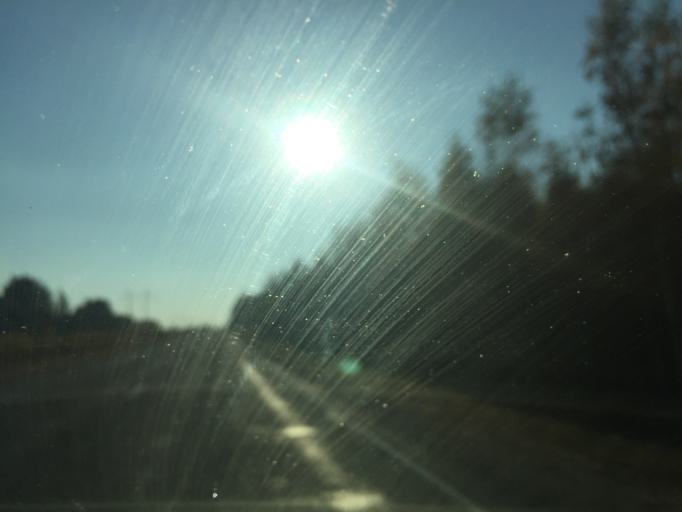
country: BY
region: Gomel
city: Dobrush
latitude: 52.3671
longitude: 31.2495
